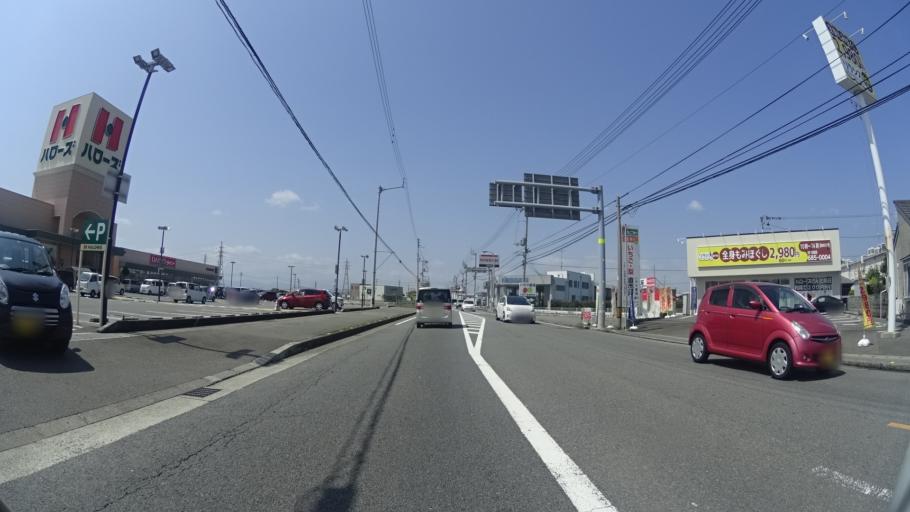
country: JP
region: Tokushima
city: Narutocho-mitsuishi
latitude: 34.1664
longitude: 134.5991
